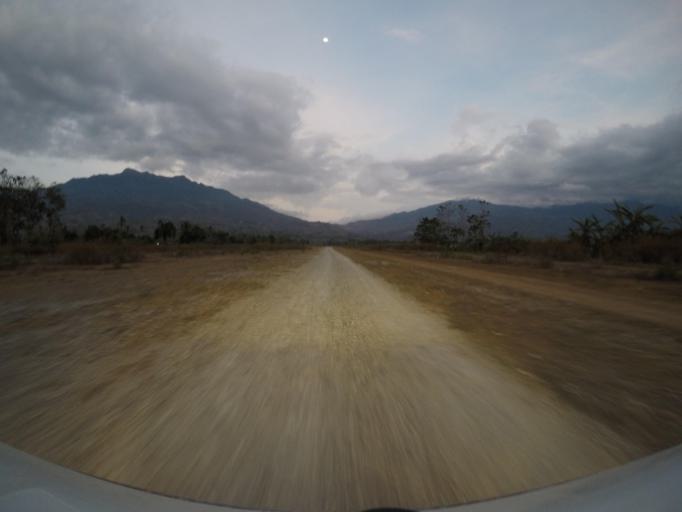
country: TL
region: Bobonaro
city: Maliana
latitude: -8.9718
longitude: 125.2139
